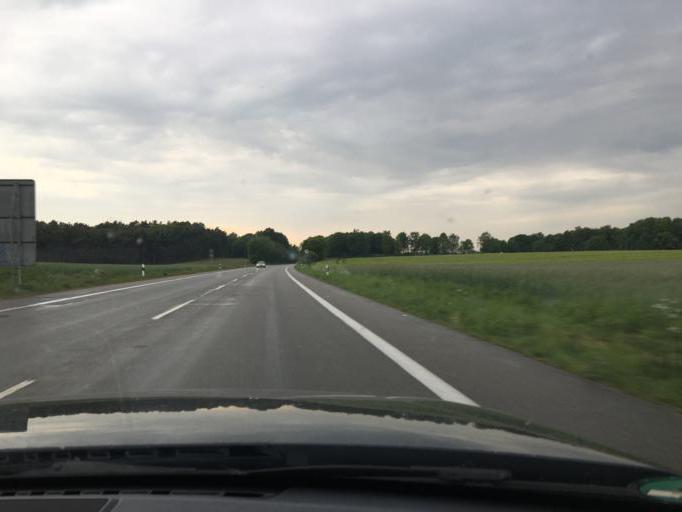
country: DE
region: North Rhine-Westphalia
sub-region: Regierungsbezirk Munster
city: Greven
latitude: 52.1146
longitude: 7.6051
